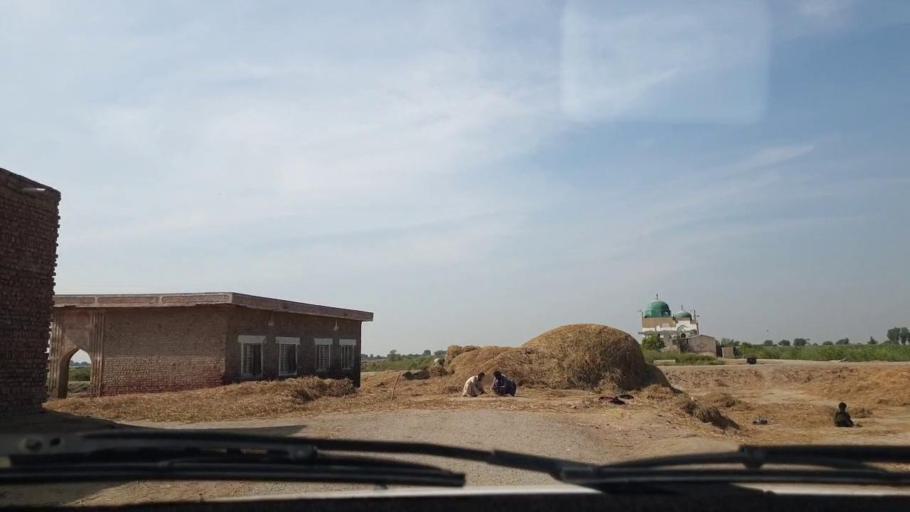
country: PK
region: Sindh
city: Bulri
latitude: 24.8638
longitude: 68.4710
